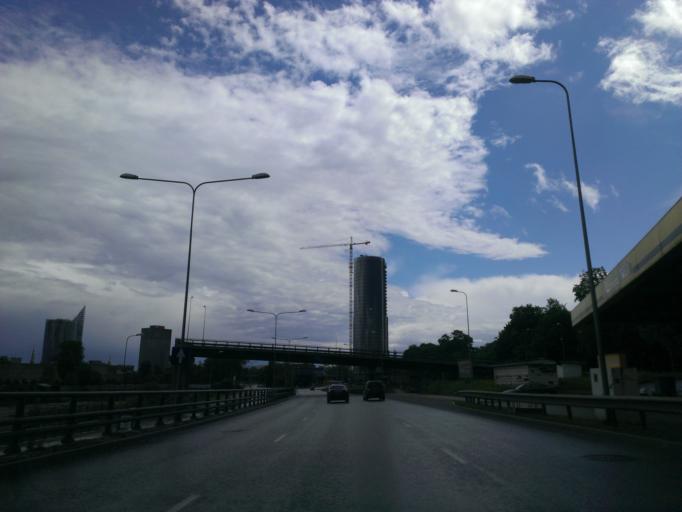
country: LV
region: Riga
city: Riga
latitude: 56.9508
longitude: 24.0729
